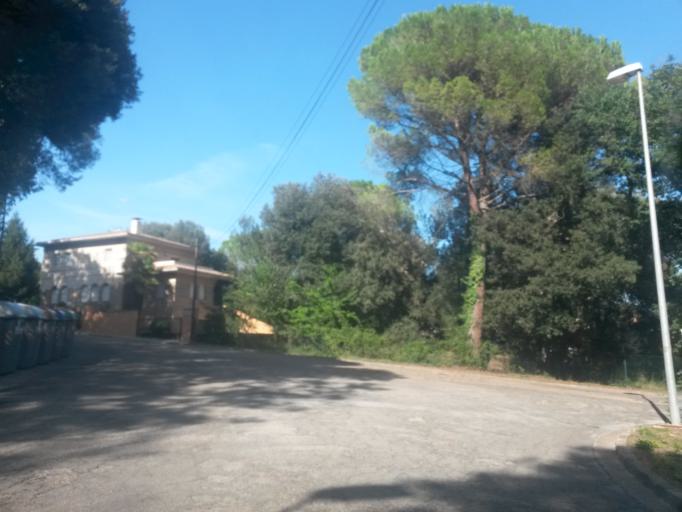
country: ES
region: Catalonia
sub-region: Provincia de Girona
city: Fornells de la Selva
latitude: 41.9492
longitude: 2.8196
